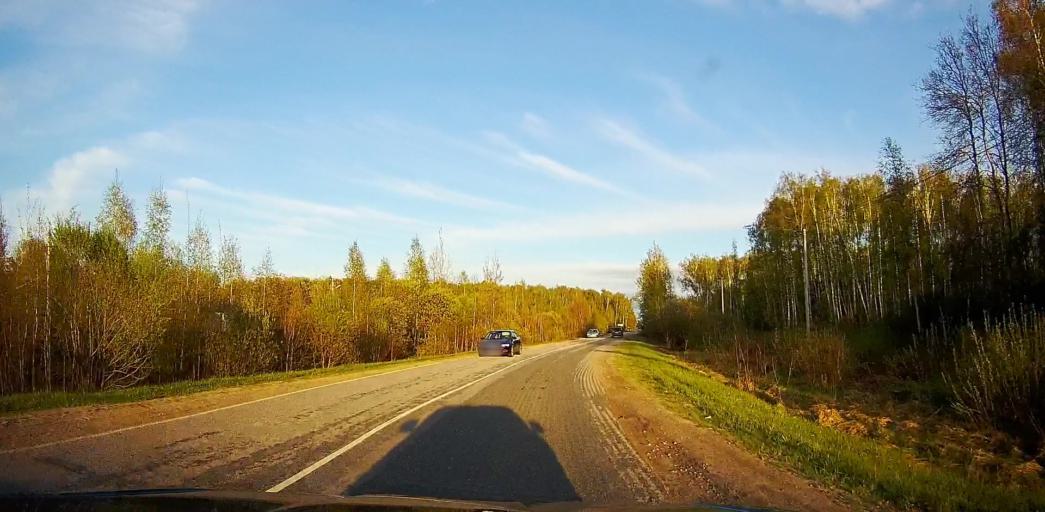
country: RU
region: Moskovskaya
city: Meshcherino
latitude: 55.2262
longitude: 38.3913
